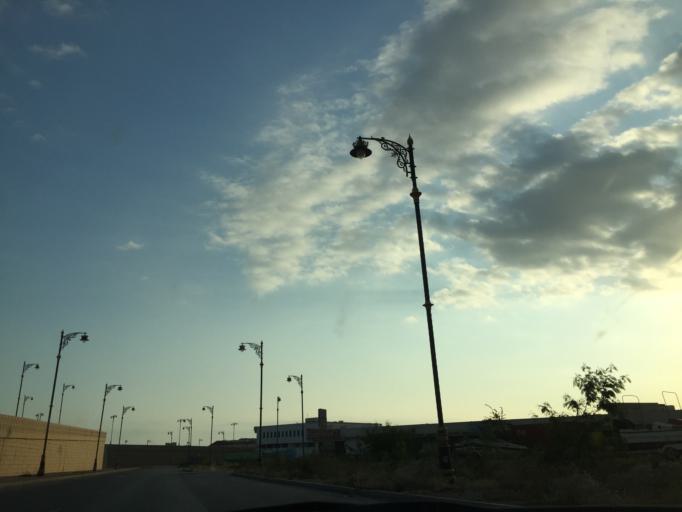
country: OM
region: Zufar
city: Salalah
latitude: 17.0188
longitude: 54.0565
